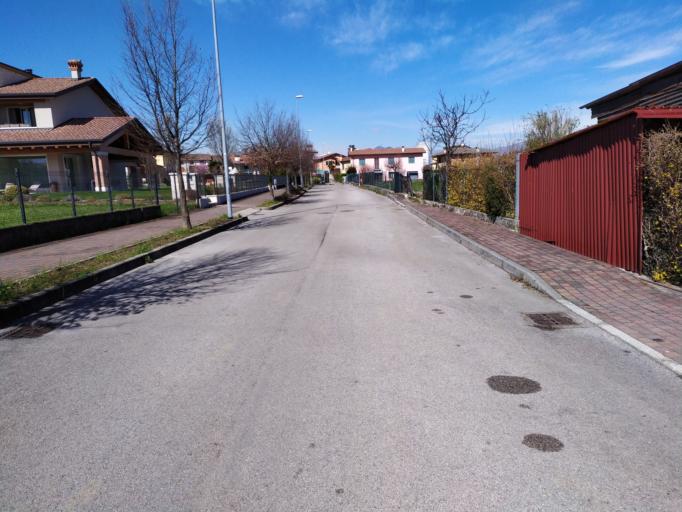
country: IT
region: Veneto
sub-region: Provincia di Vicenza
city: Caldogno-Rettorgole-Cresole
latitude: 45.6045
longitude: 11.4964
